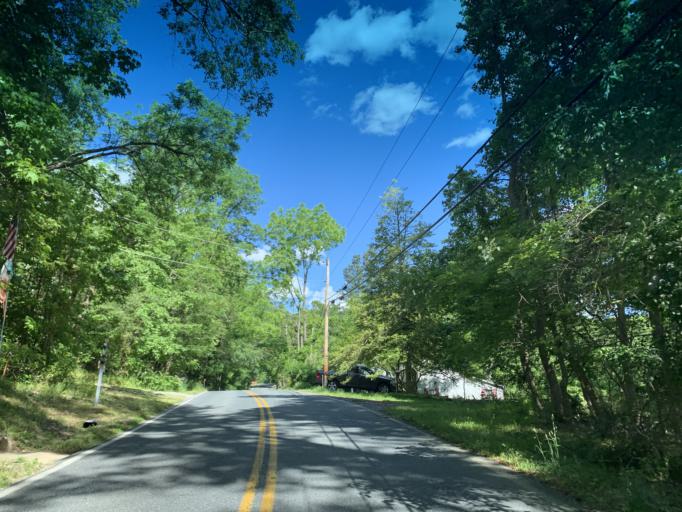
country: US
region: Maryland
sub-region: Cecil County
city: Charlestown
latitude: 39.5421
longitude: -75.9271
